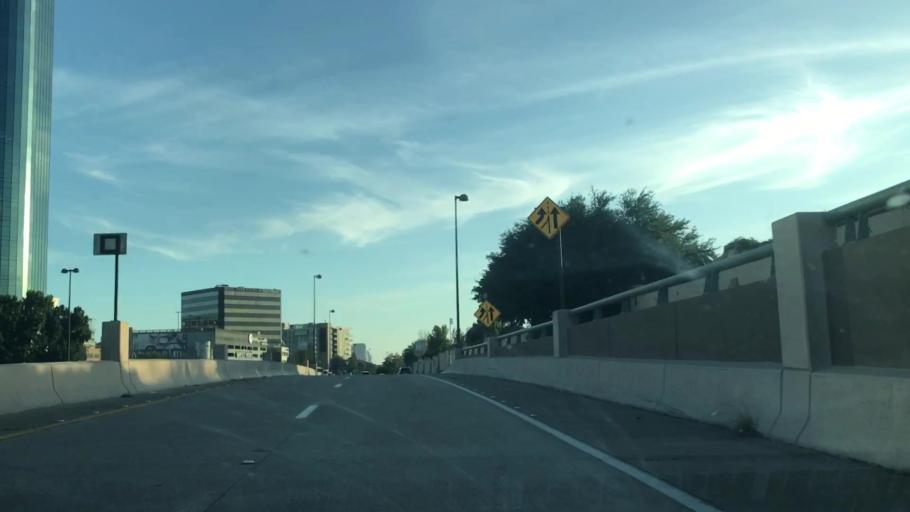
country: US
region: Texas
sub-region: Dallas County
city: Highland Park
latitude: 32.8409
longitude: -96.7764
